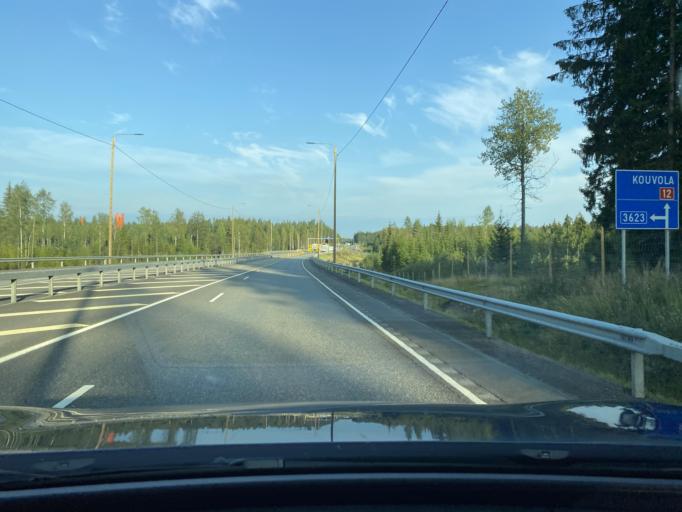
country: FI
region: Kymenlaakso
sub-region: Kouvola
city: Kouvola
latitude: 60.8685
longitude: 26.5454
